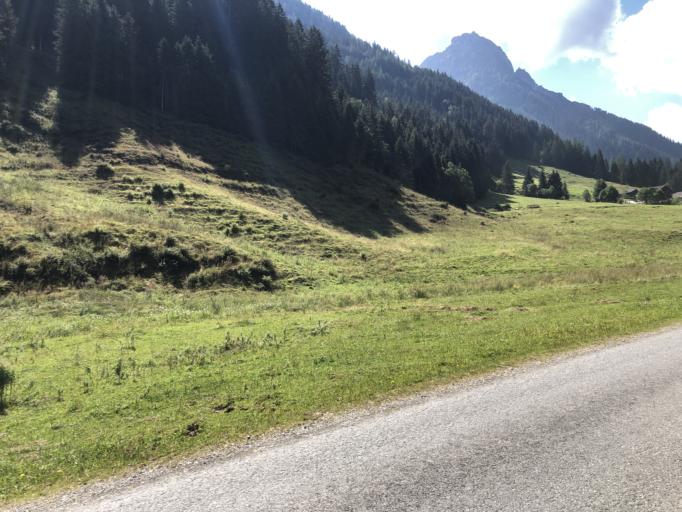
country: AT
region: Tyrol
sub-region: Politischer Bezirk Kitzbuhel
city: Kirchberg in Tirol
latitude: 47.3588
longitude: 12.2903
